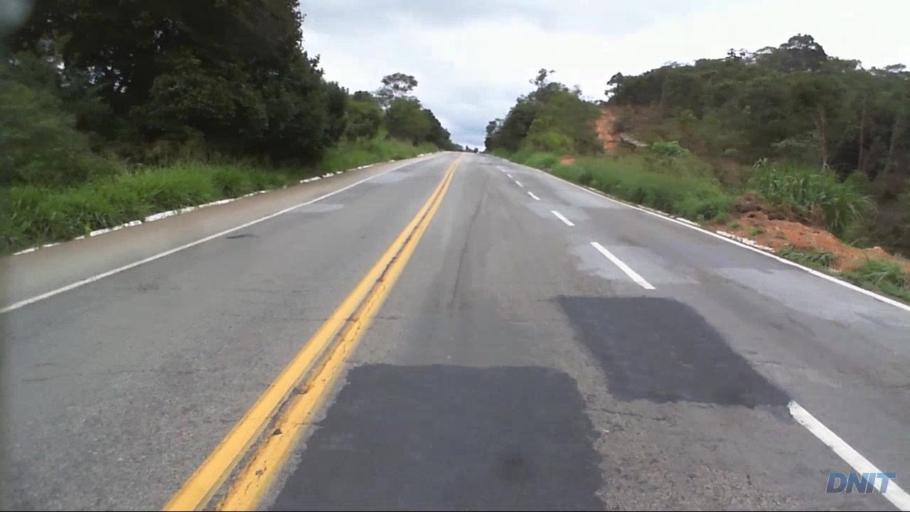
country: BR
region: Minas Gerais
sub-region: Barao De Cocais
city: Barao de Cocais
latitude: -19.7973
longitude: -43.4177
